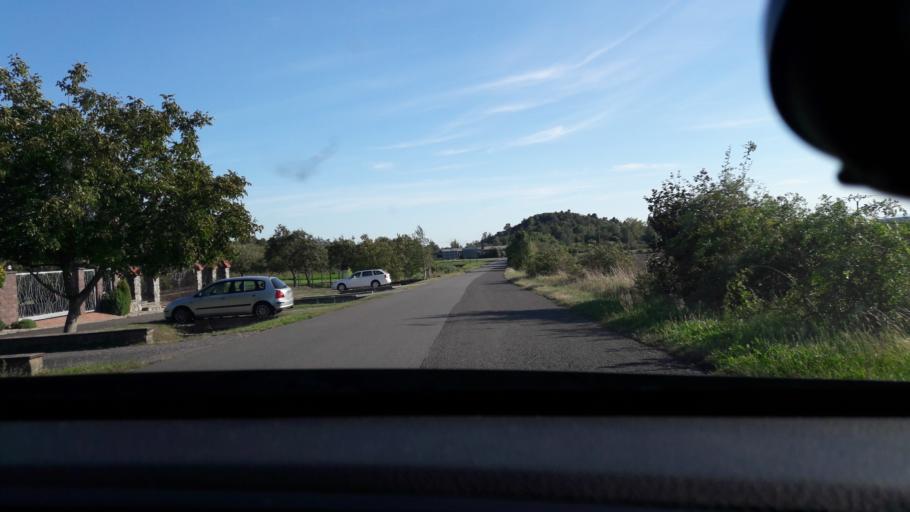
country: SK
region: Kosicky
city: Vinne
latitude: 48.8029
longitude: 21.9711
